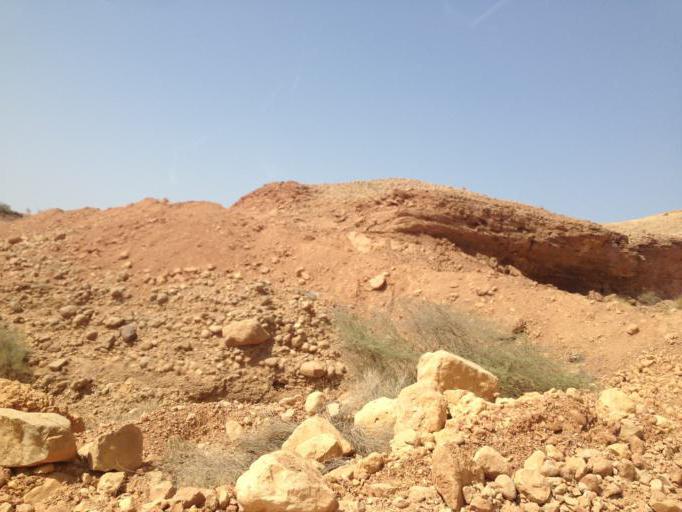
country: OM
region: Ash Sharqiyah
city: Ibra'
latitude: 23.0738
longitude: 58.8866
